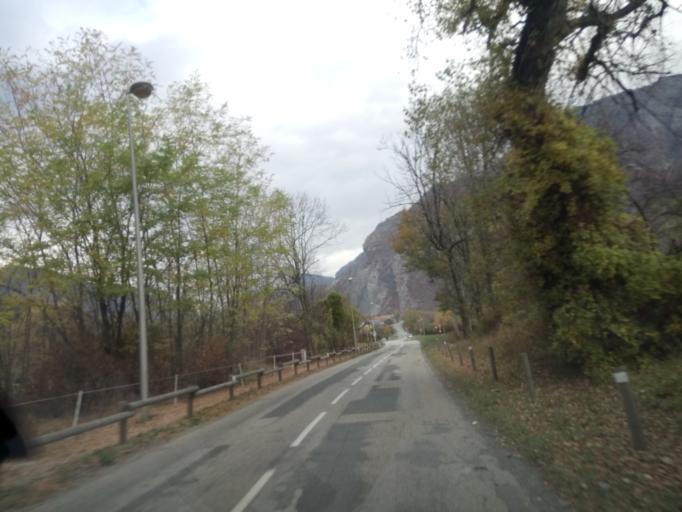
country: FR
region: Rhone-Alpes
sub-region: Departement de la Savoie
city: Villargondran
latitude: 45.2552
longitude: 6.3844
